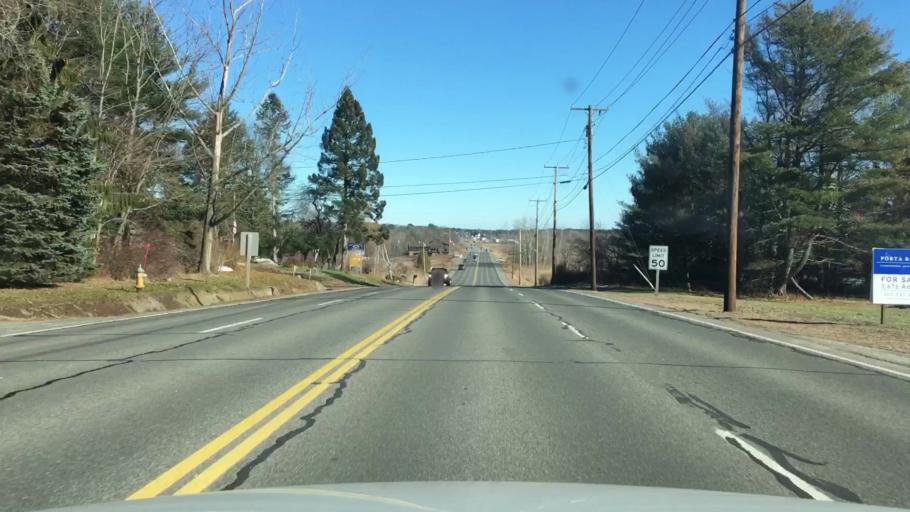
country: US
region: Maine
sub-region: Cumberland County
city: West Scarborough
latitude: 43.5744
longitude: -70.3821
